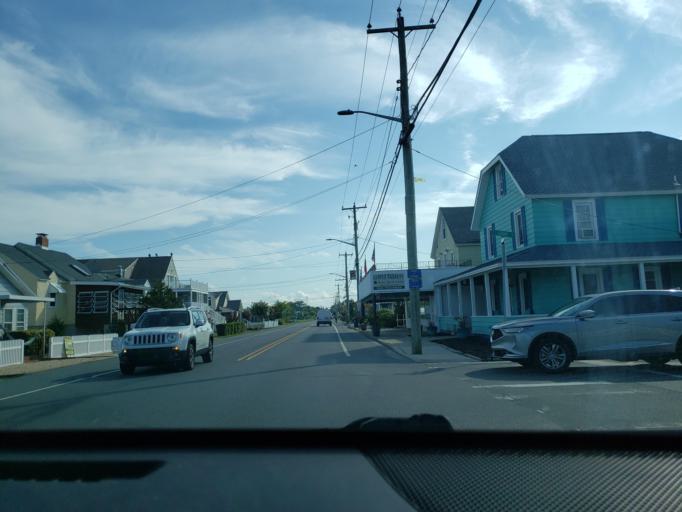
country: US
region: Delaware
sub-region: Sussex County
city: Lewes
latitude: 38.7800
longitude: -75.1332
